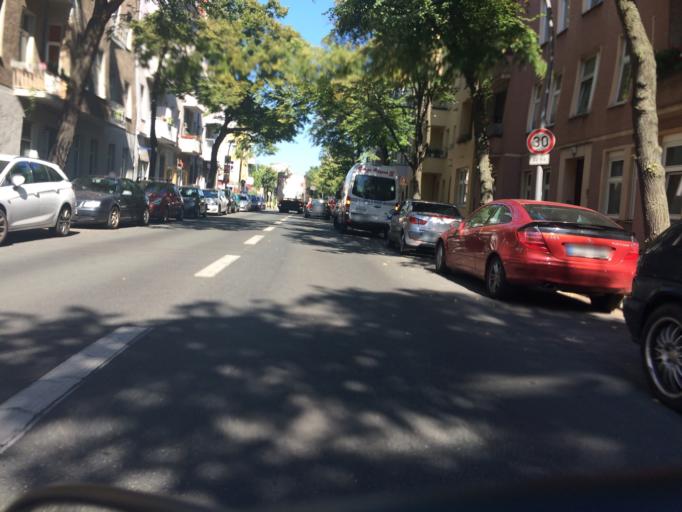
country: DE
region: Berlin
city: Wilhelmsruh
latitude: 52.5707
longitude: 13.3798
